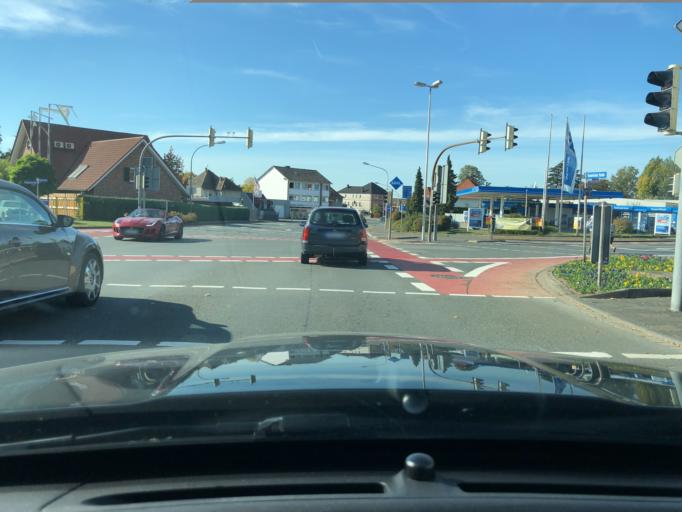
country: DE
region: North Rhine-Westphalia
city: Lengerich
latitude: 52.1863
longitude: 7.8629
